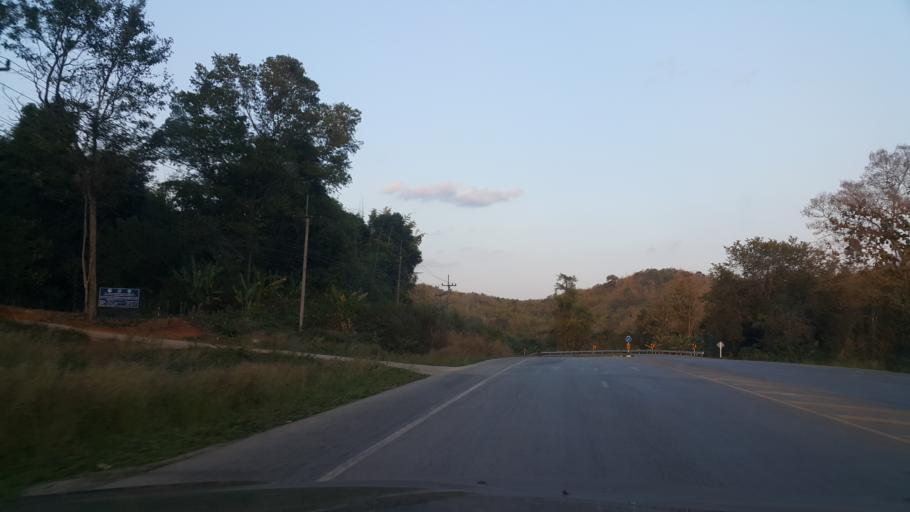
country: TH
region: Loei
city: Loei
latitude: 17.4866
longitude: 101.6109
